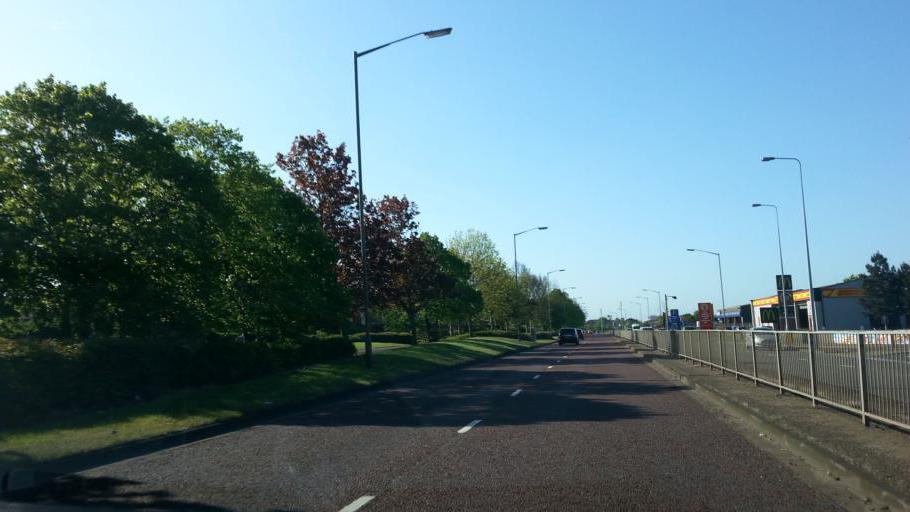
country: GB
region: England
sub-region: Peterborough
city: Peterborough
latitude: 52.5819
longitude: -0.2519
